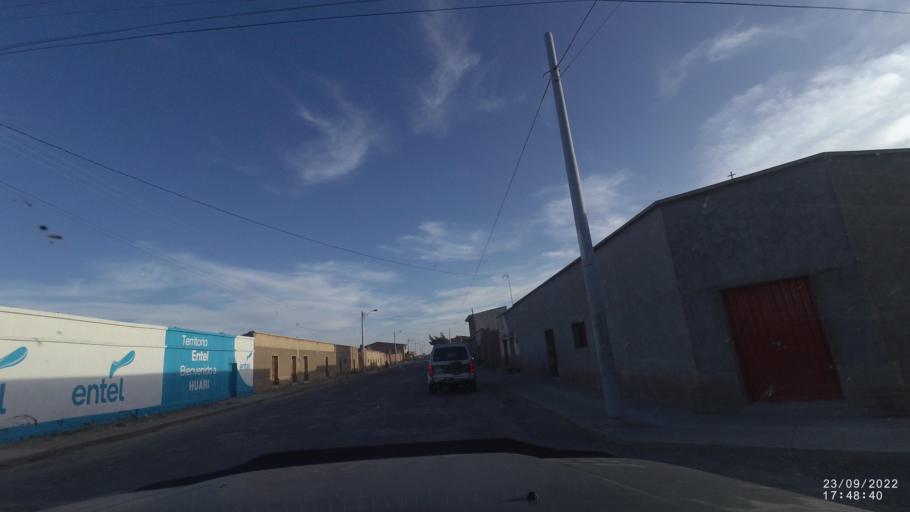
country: BO
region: Oruro
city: Challapata
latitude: -19.0175
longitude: -66.7773
